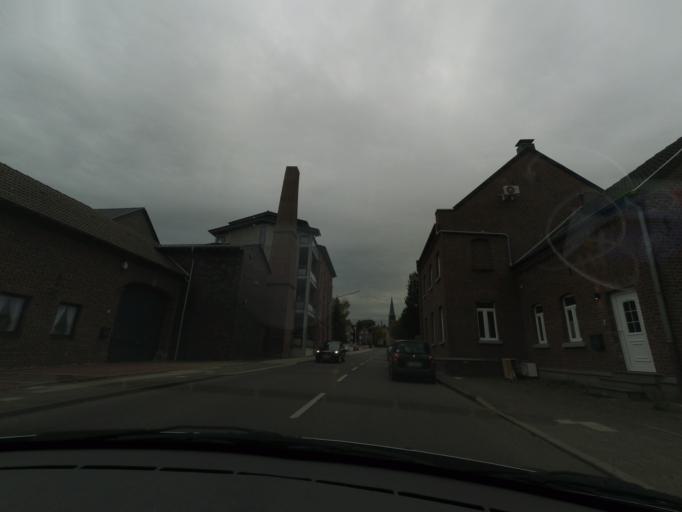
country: DE
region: North Rhine-Westphalia
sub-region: Regierungsbezirk Dusseldorf
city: Korschenbroich
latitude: 51.1676
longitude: 6.5397
